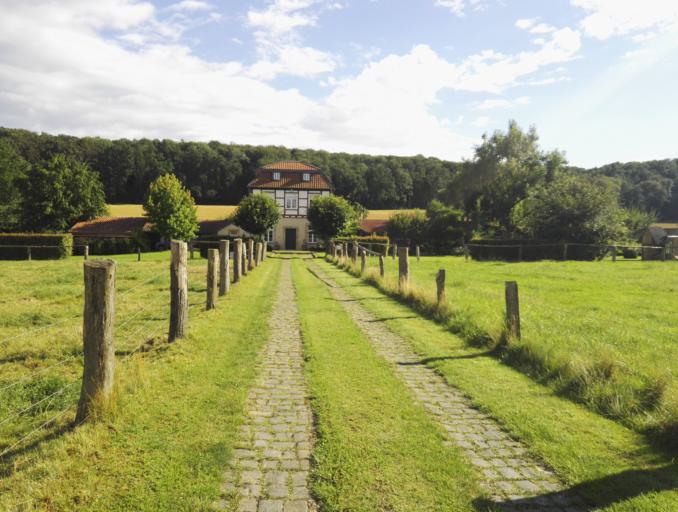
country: DE
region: Lower Saxony
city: Holle
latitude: 52.0943
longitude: 10.1329
